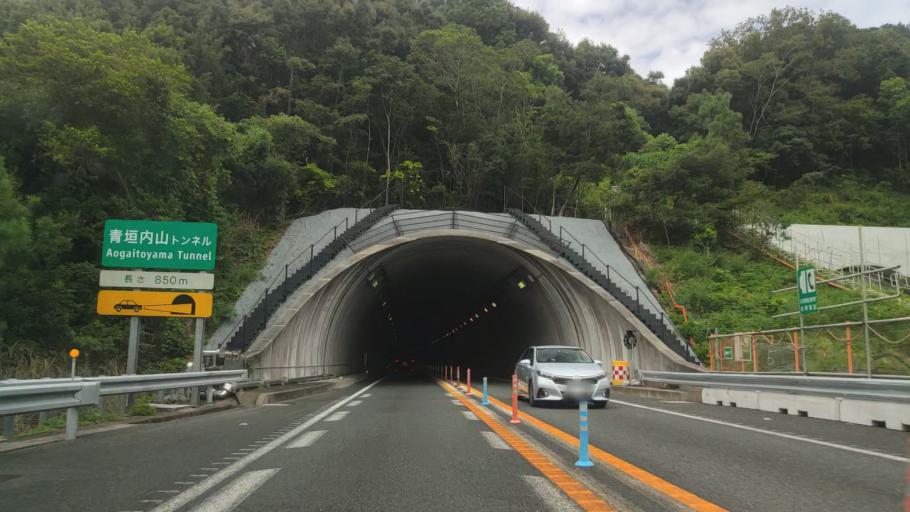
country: JP
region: Wakayama
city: Gobo
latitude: 33.8490
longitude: 135.2165
